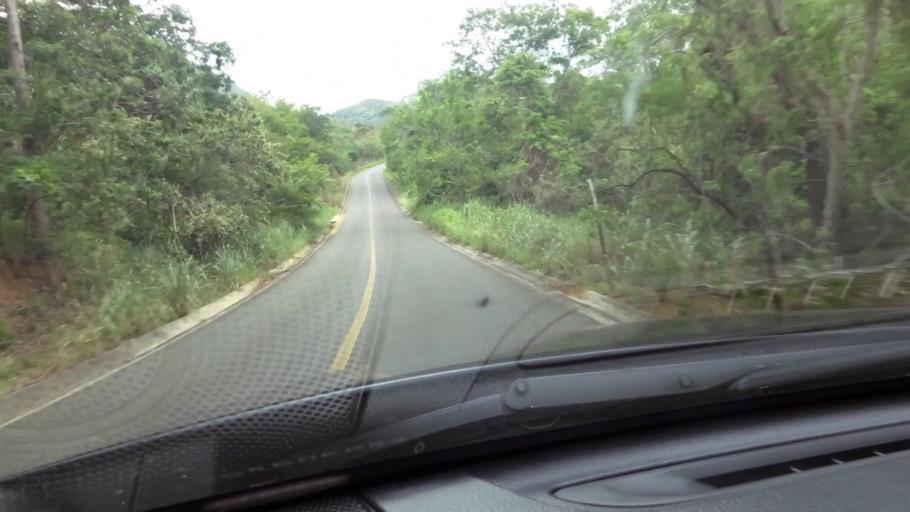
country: BR
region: Espirito Santo
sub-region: Guarapari
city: Guarapari
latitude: -20.6130
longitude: -40.5325
